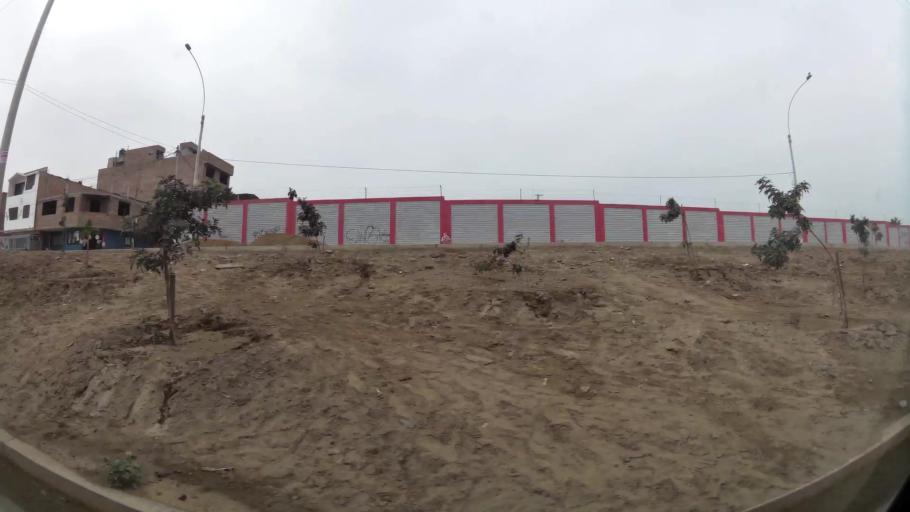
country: PE
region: Lima
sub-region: Lima
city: Surco
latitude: -12.2201
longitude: -76.9495
